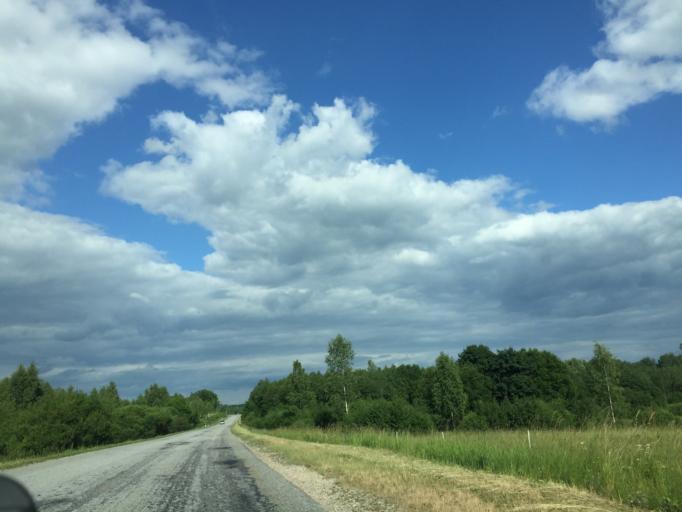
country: LV
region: Ogre
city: Jumprava
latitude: 56.7998
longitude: 25.0555
